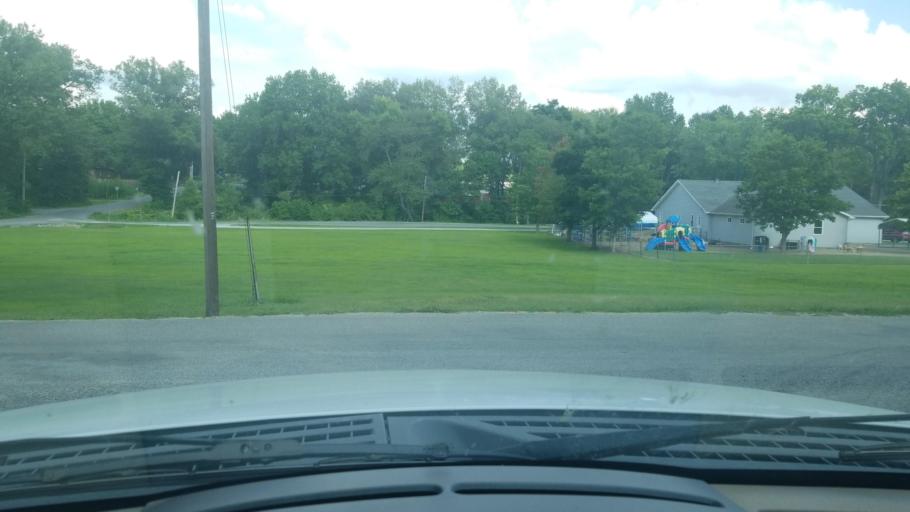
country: US
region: Illinois
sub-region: Saline County
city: Eldorado
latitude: 37.8193
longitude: -88.4397
